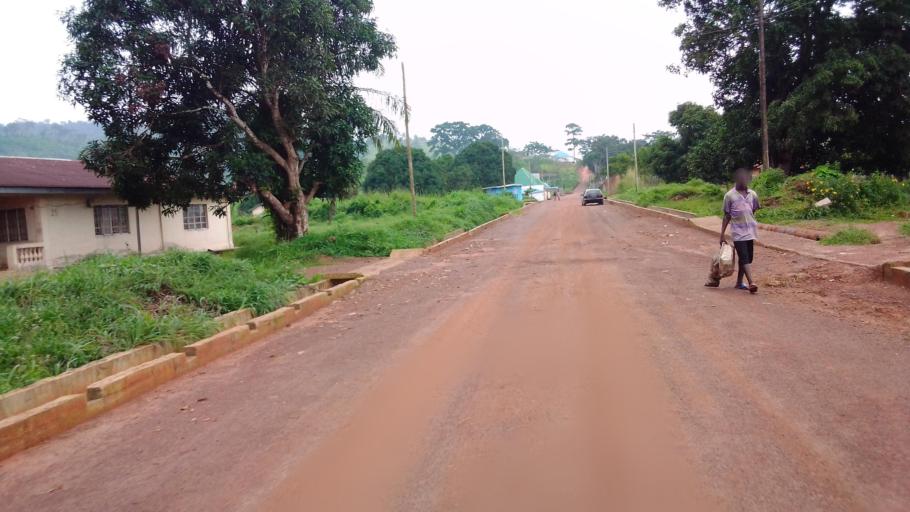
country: SL
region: Eastern Province
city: Kenema
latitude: 7.8896
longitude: -11.1915
